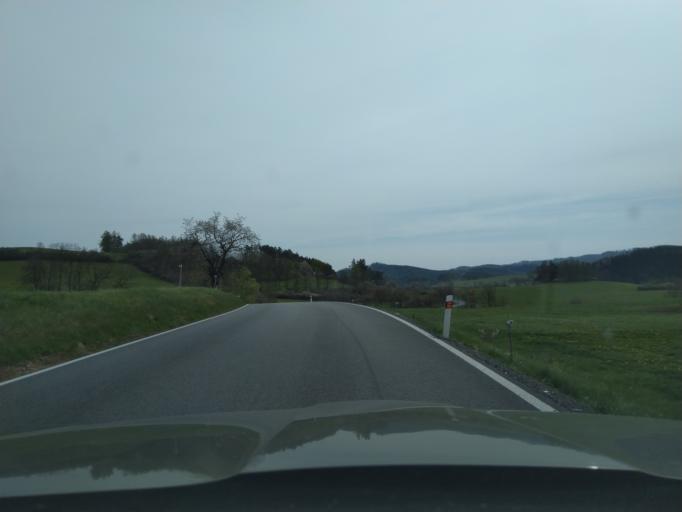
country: CZ
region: Jihocesky
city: Ckyne
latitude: 49.1176
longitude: 13.8113
